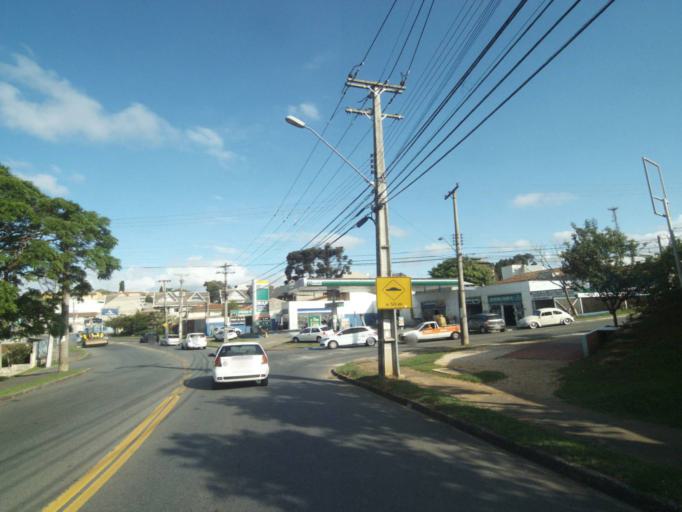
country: BR
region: Parana
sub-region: Curitiba
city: Curitiba
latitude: -25.3934
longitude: -49.2956
